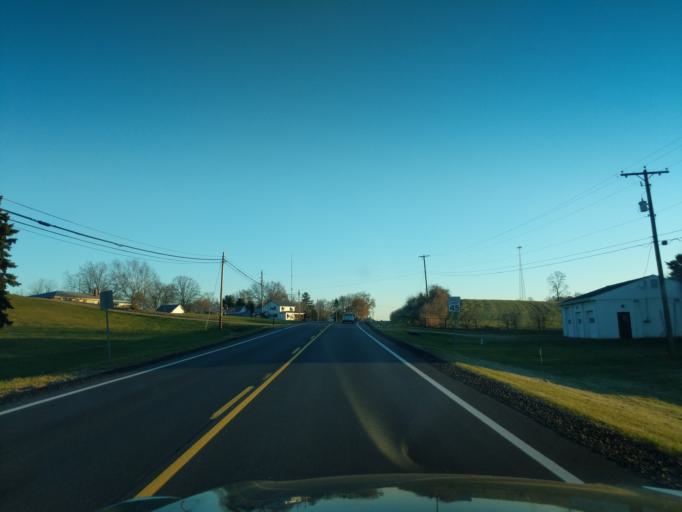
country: US
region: Ohio
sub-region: Licking County
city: Harbor Hills
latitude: 39.9561
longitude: -82.4129
